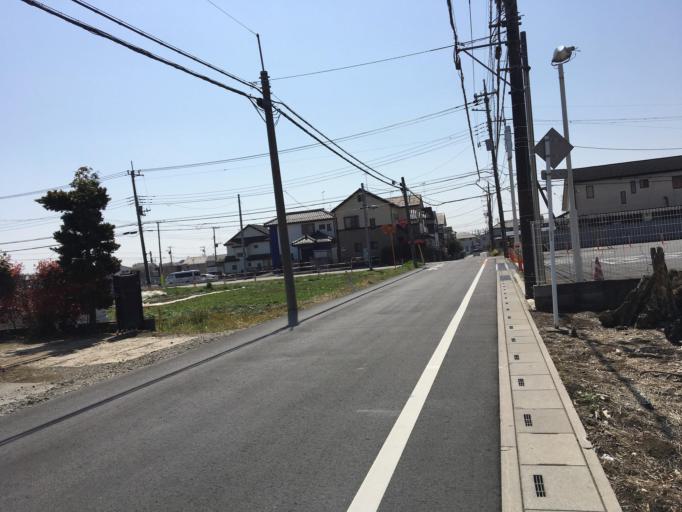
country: JP
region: Saitama
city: Sakado
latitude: 35.9074
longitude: 139.3660
